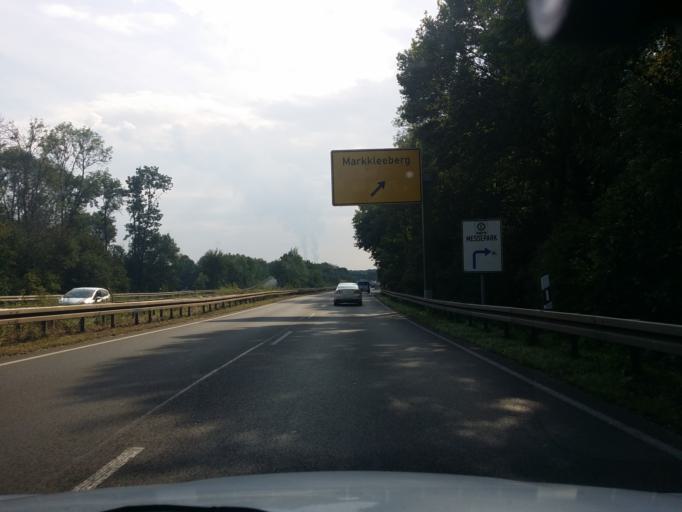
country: DE
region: Saxony
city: Markkleeberg
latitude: 51.2762
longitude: 12.3832
